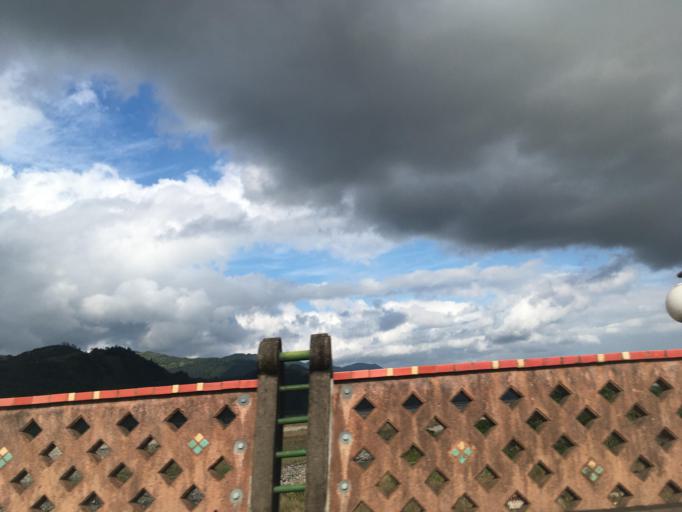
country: TW
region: Taiwan
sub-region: Yilan
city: Yilan
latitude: 24.6682
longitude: 121.6121
